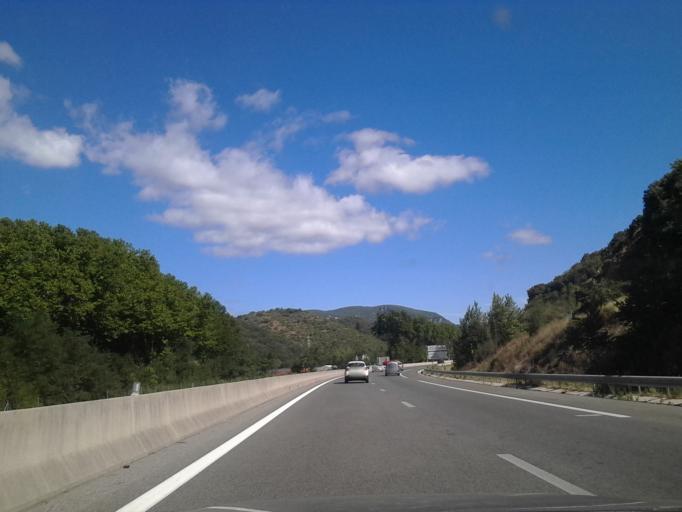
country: FR
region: Languedoc-Roussillon
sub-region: Departement de l'Herault
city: Lodeve
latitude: 43.7104
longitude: 3.3254
